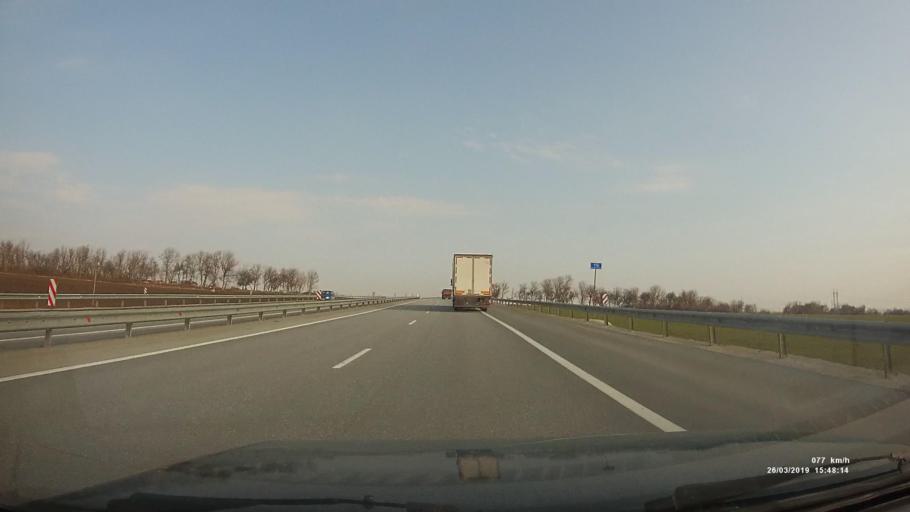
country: RU
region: Rostov
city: Chaltyr
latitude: 47.2798
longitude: 39.4489
